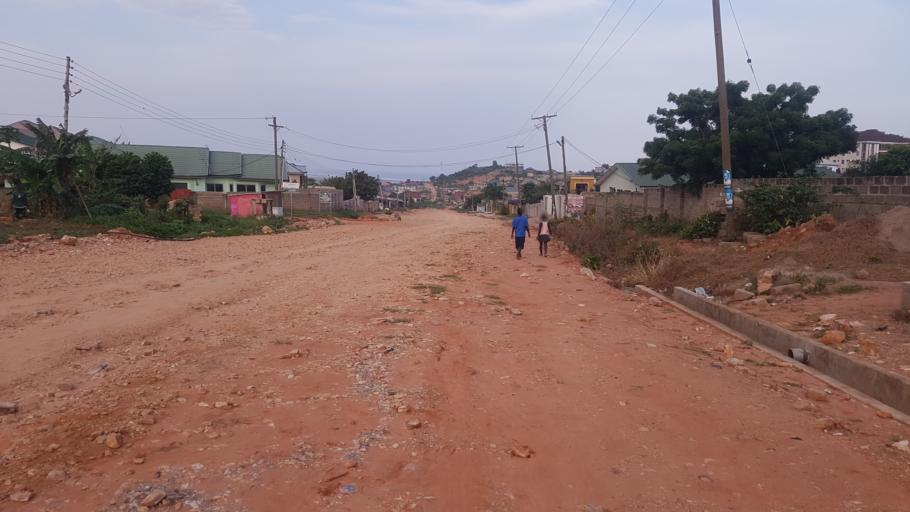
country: GH
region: Greater Accra
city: Gbawe
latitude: 5.5239
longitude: -0.3464
